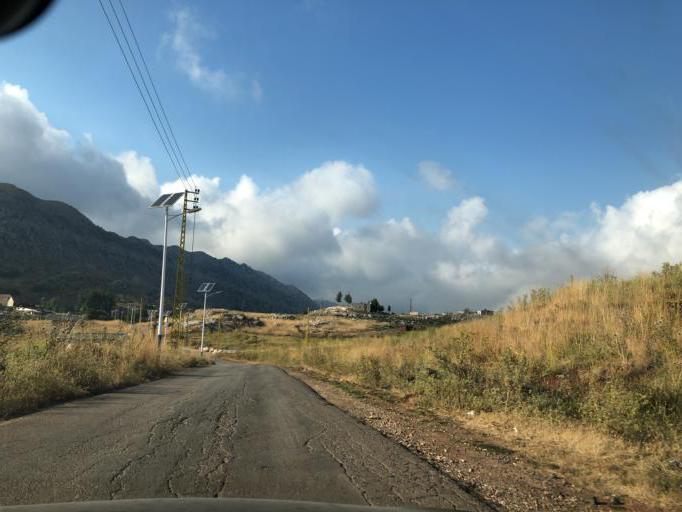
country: LB
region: Liban-Nord
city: Amioun
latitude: 34.1422
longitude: 35.8594
